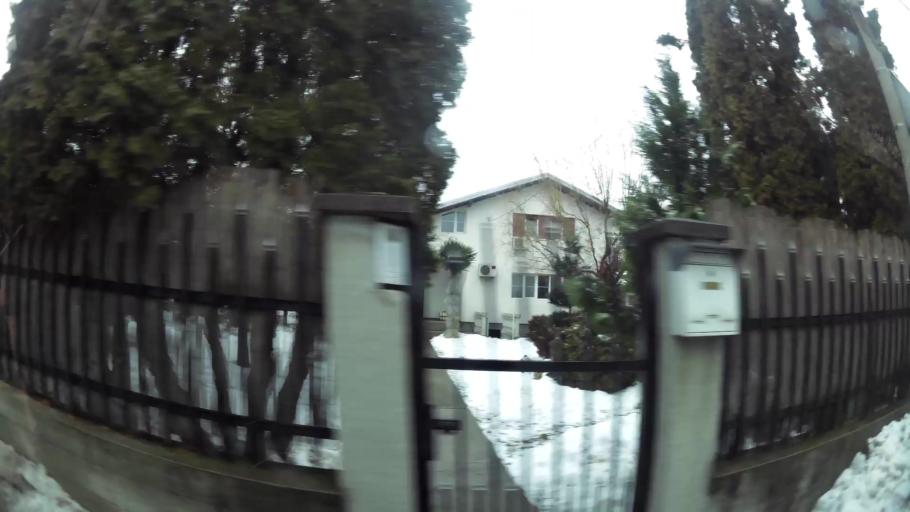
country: RS
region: Central Serbia
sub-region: Belgrade
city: Zemun
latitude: 44.8420
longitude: 20.3611
